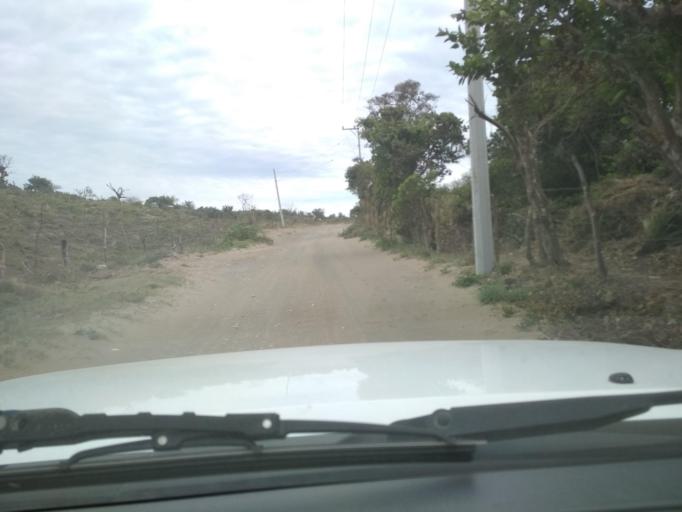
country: MX
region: Veracruz
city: Anton Lizardo
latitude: 19.0493
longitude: -95.9927
